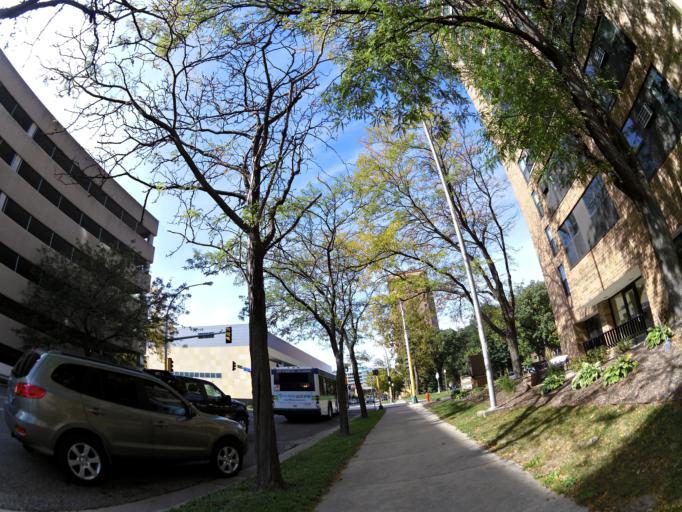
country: US
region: Minnesota
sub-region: Olmsted County
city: Rochester
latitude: 44.0255
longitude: -92.4643
